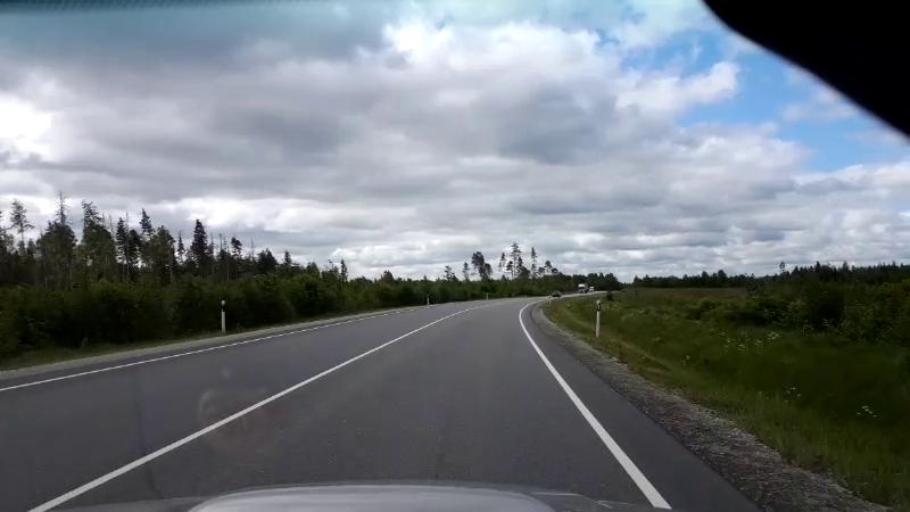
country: EE
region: Raplamaa
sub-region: Maerjamaa vald
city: Marjamaa
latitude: 58.9614
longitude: 24.4760
